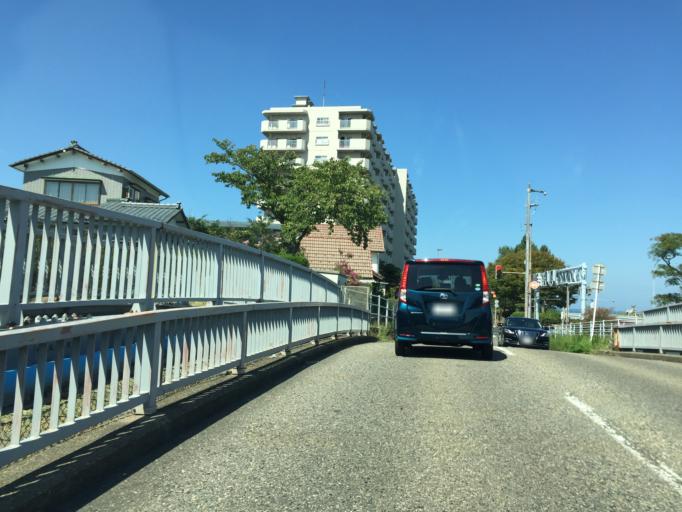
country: JP
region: Niigata
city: Niigata-shi
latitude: 37.9004
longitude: 139.0067
